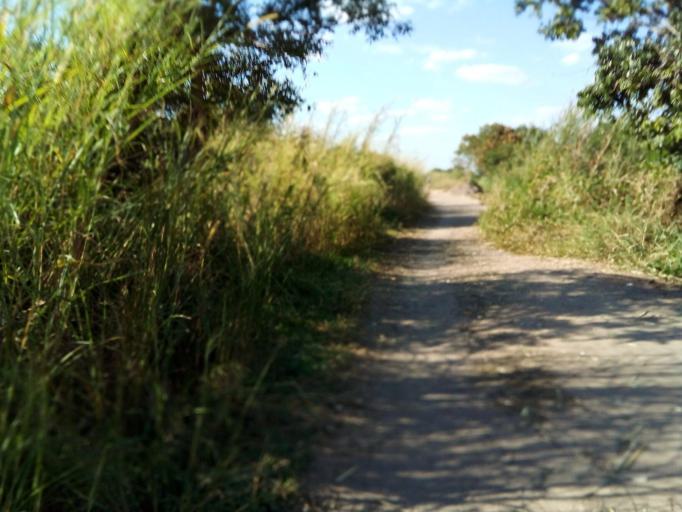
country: MZ
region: Zambezia
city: Quelimane
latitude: -17.5878
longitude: 36.8386
